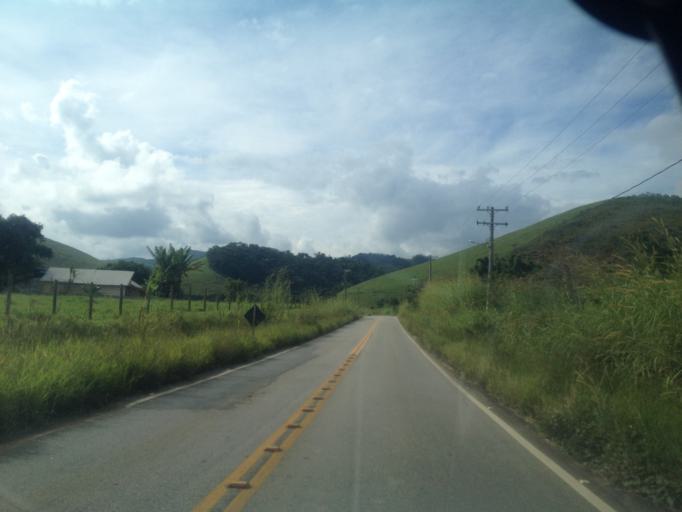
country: BR
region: Rio de Janeiro
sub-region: Quatis
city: Quatis
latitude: -22.3551
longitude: -44.2453
